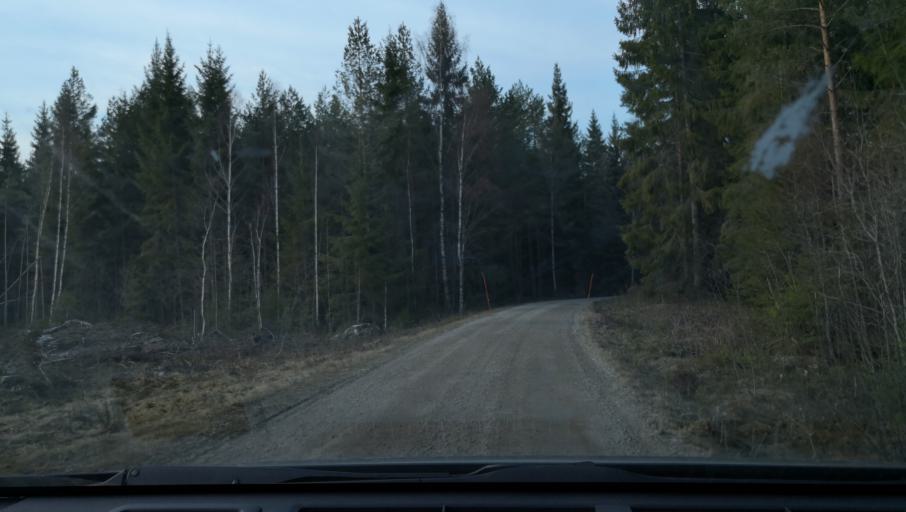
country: SE
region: OErebro
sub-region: Lindesbergs Kommun
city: Frovi
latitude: 59.3794
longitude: 15.3610
